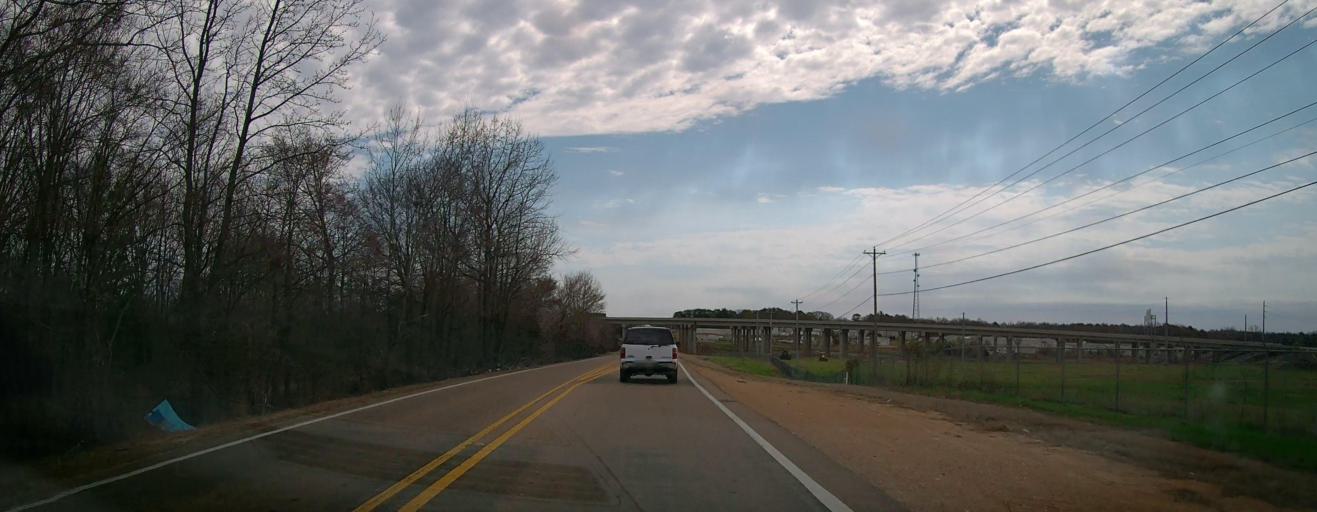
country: US
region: Mississippi
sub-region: Marshall County
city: Byhalia
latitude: 34.8852
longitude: -89.7217
